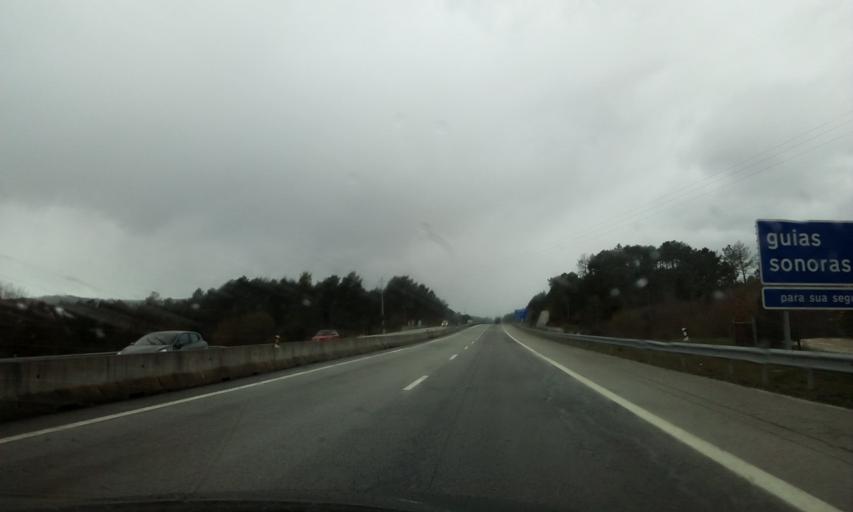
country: PT
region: Guarda
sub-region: Fornos de Algodres
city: Fornos de Algodres
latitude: 40.6146
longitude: -7.6285
